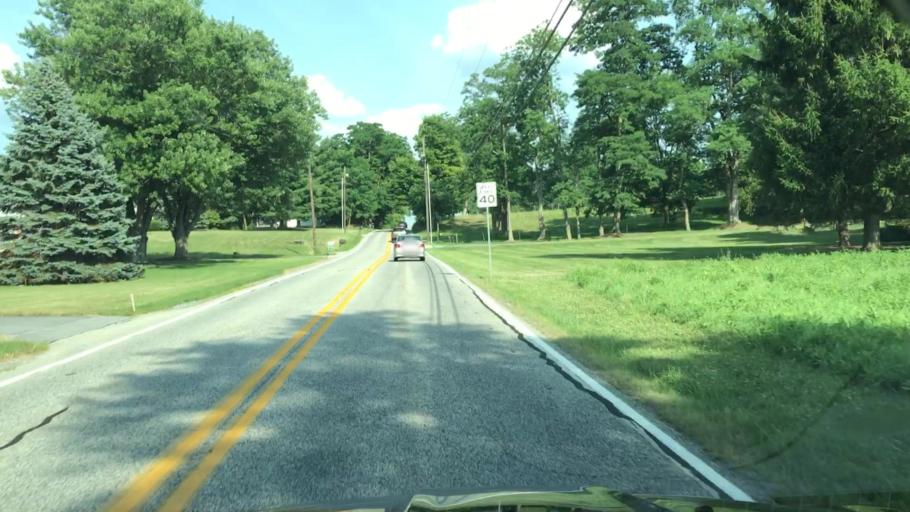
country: US
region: Pennsylvania
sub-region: Cumberland County
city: Boiling Springs
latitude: 40.1769
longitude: -77.0771
